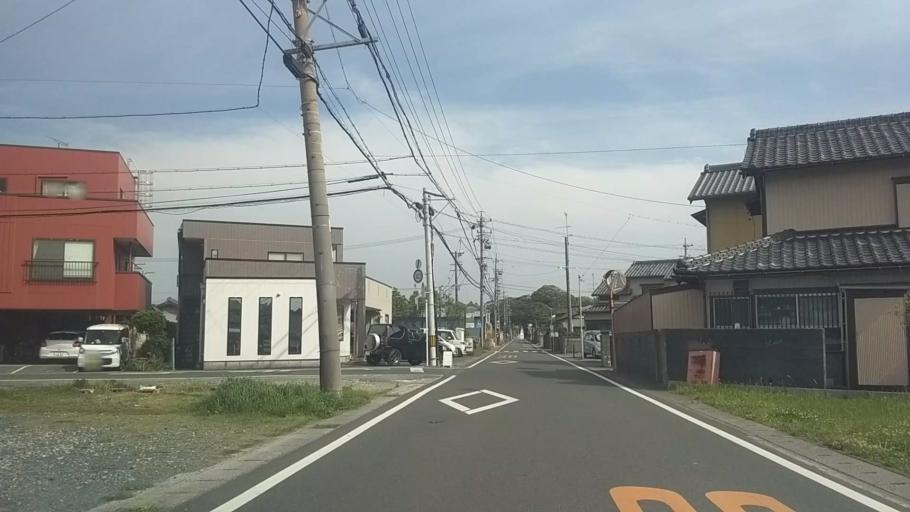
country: JP
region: Shizuoka
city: Kosai-shi
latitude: 34.7068
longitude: 137.6274
